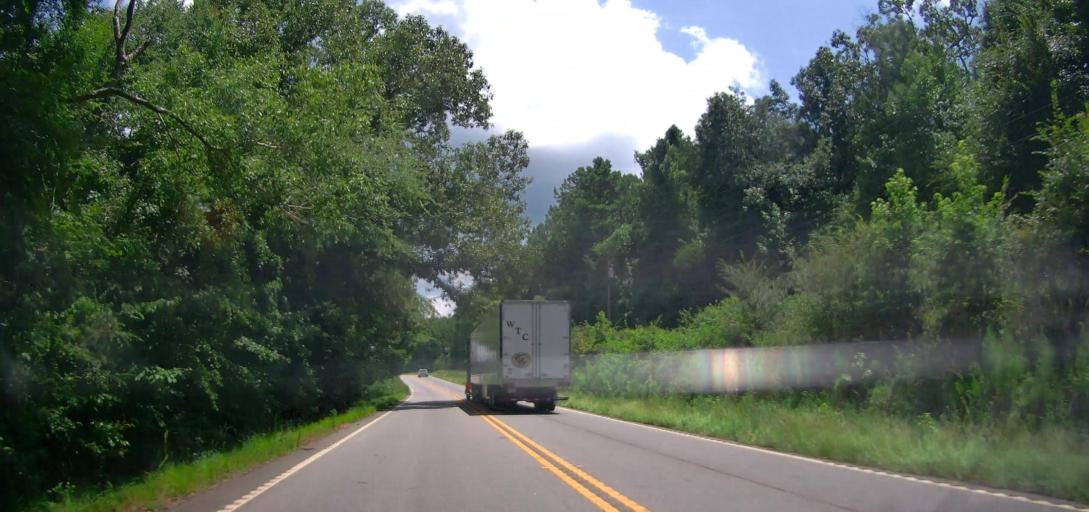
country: US
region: Georgia
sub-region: Meriwether County
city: Greenville
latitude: 33.0250
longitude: -84.6867
